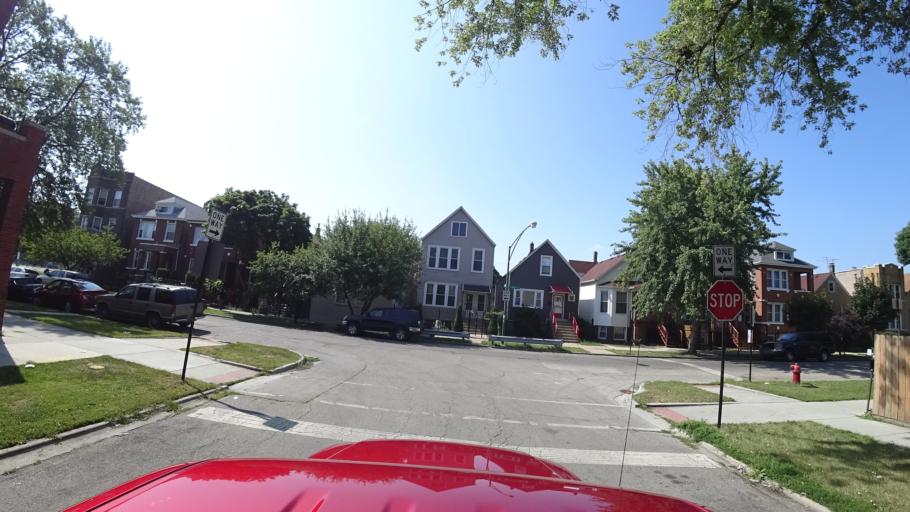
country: US
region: Illinois
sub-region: Cook County
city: Chicago
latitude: 41.8122
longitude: -87.6858
